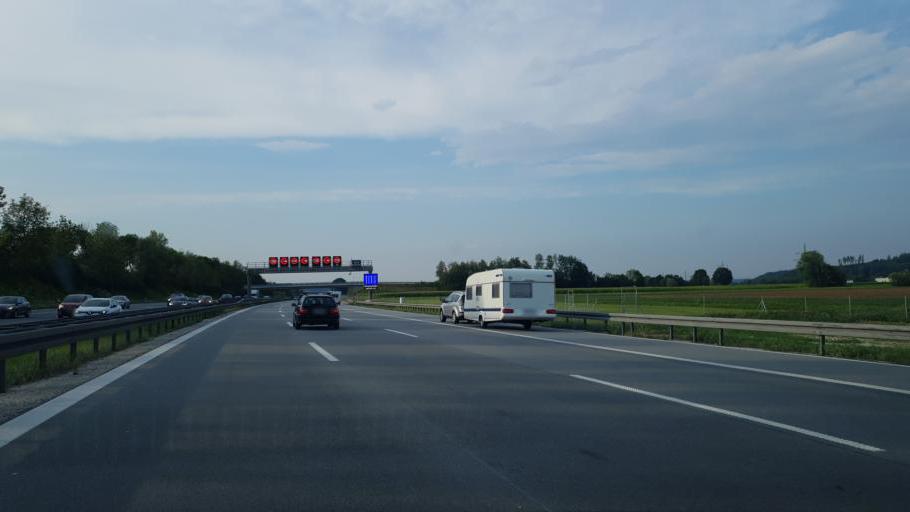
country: DE
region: Bavaria
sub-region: Upper Bavaria
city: Kranzberg
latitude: 48.4029
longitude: 11.5900
